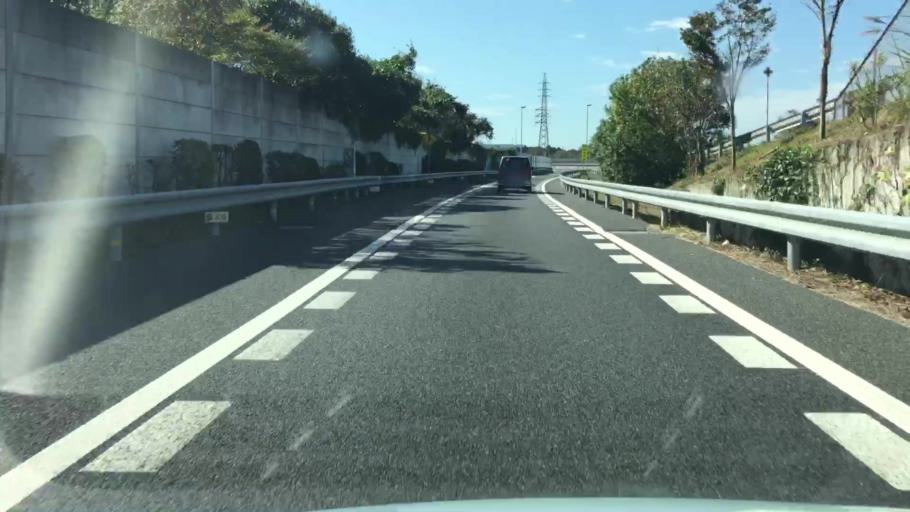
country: JP
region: Ibaraki
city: Naka
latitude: 36.0332
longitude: 140.1284
